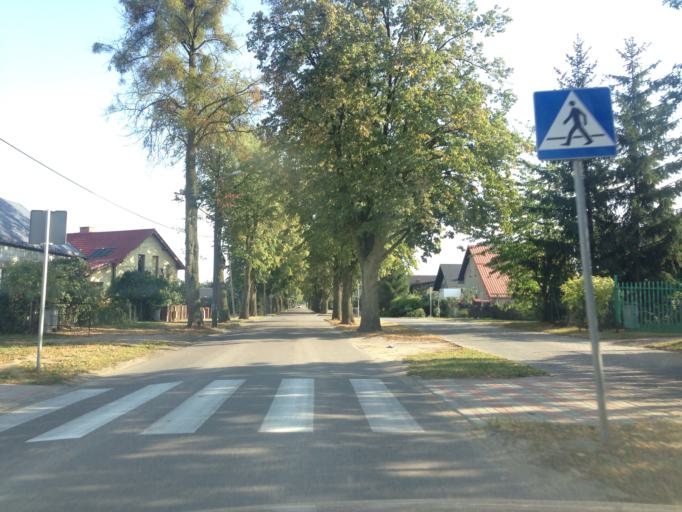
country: PL
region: Warmian-Masurian Voivodeship
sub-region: Powiat ilawski
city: Ilawa
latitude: 53.6155
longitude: 19.5681
